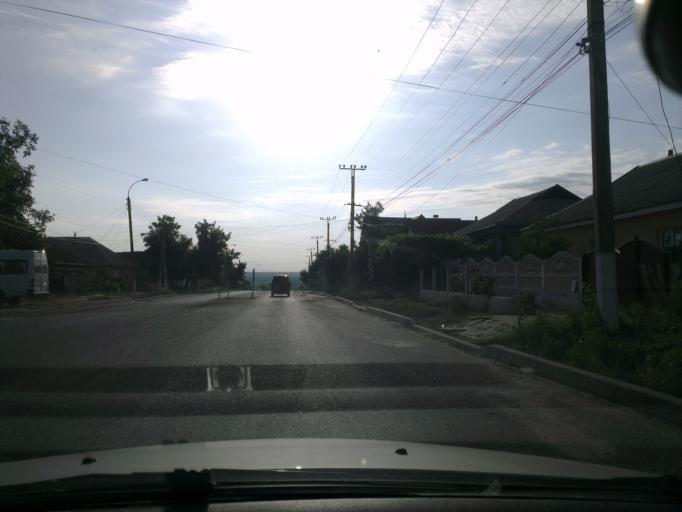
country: MD
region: Cahul
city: Cahul
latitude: 45.9200
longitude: 28.2004
